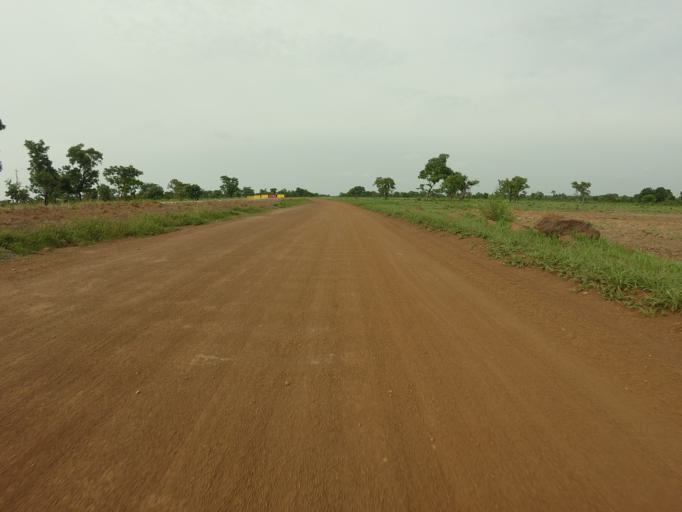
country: GH
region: Northern
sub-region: Yendi
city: Yendi
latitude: 9.7865
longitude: -0.1161
